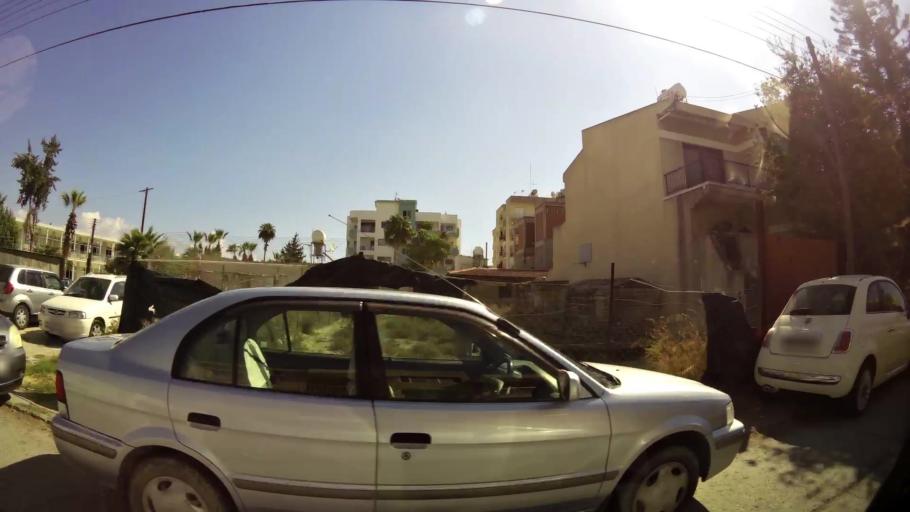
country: CY
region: Larnaka
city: Larnaca
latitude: 34.9261
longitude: 33.6289
